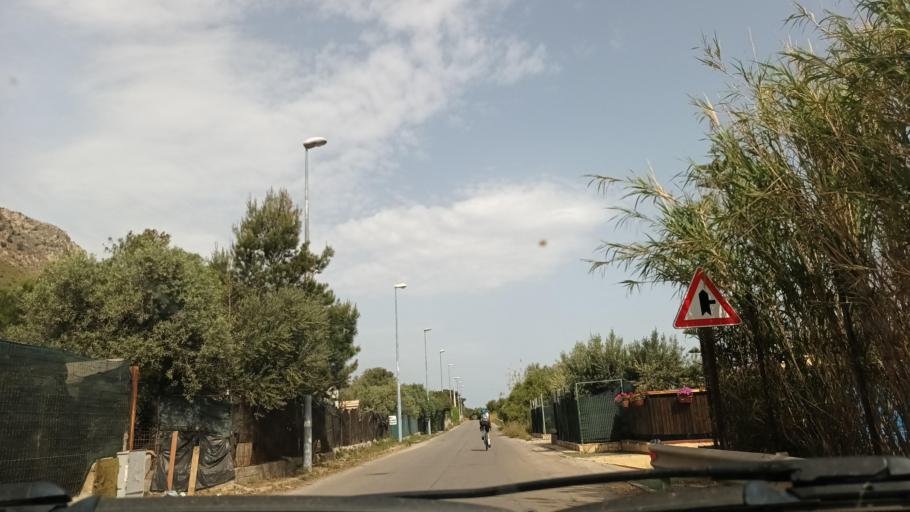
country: IT
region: Sicily
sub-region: Palermo
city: Santa Flavia
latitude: 38.1082
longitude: 13.5325
